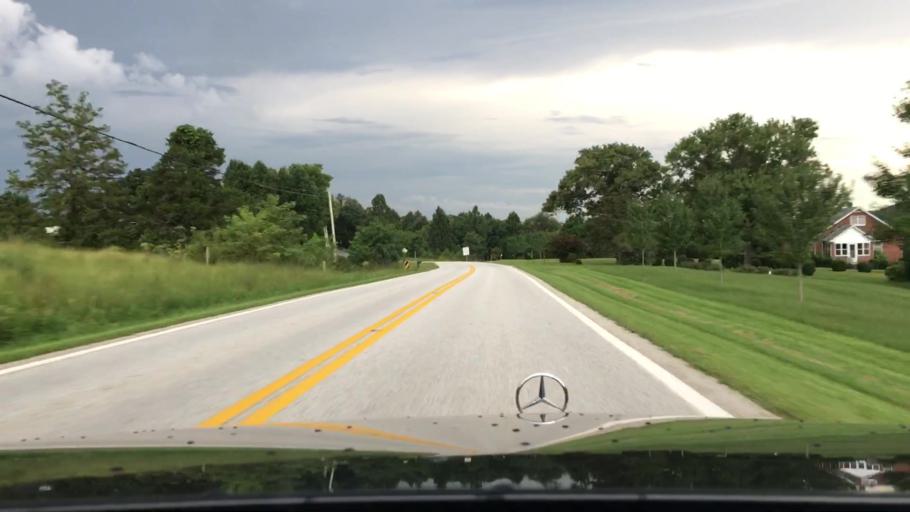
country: US
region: Virginia
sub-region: Nelson County
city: Lovingston
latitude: 37.7879
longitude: -78.9767
